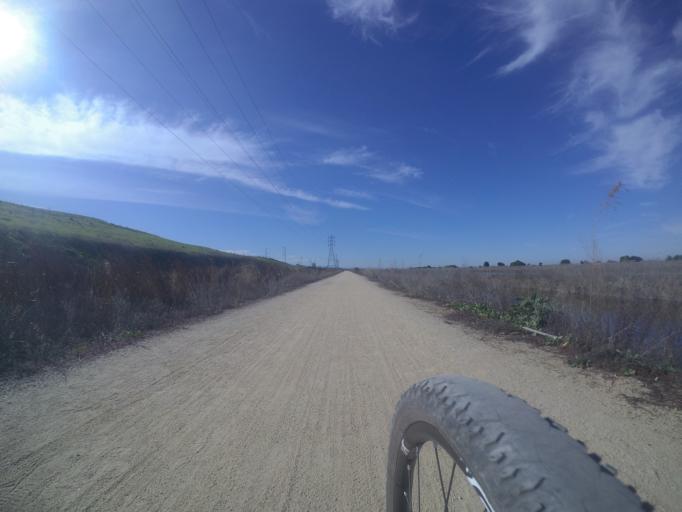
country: US
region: California
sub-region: Santa Clara County
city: Sunnyvale
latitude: 37.4212
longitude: -122.0205
